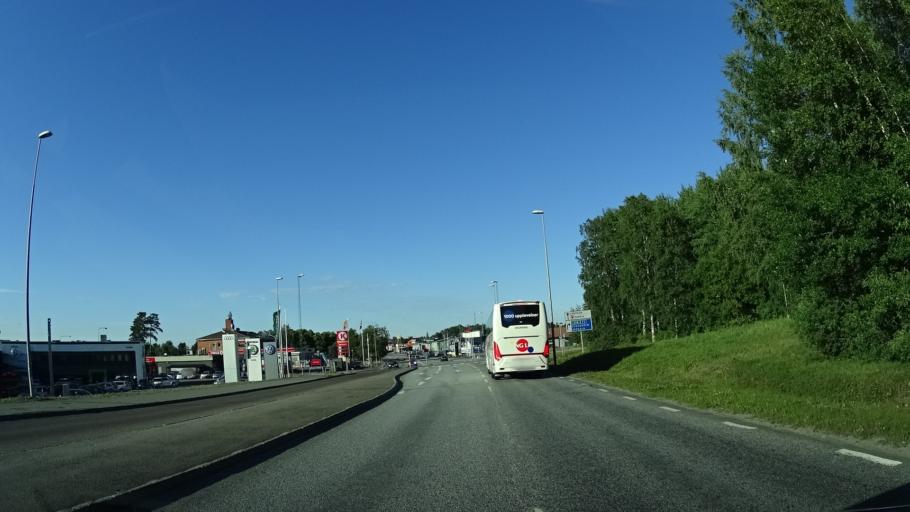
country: SE
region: Stockholm
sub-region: Norrtalje Kommun
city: Norrtalje
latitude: 59.7486
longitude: 18.6875
